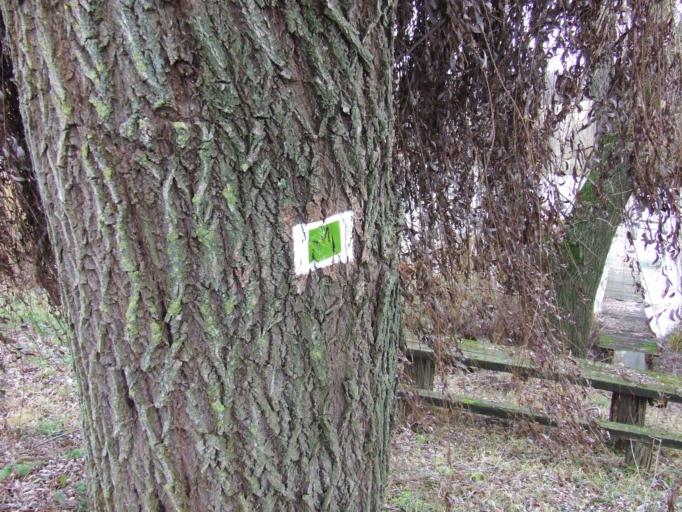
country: HU
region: Somogy
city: Tab
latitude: 46.7814
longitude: 17.9982
